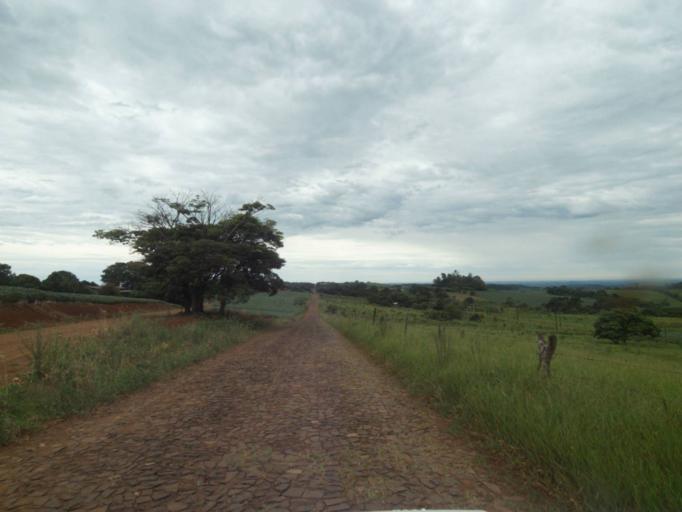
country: BR
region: Parana
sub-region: Guaraniacu
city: Guaraniacu
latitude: -24.9273
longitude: -52.9385
